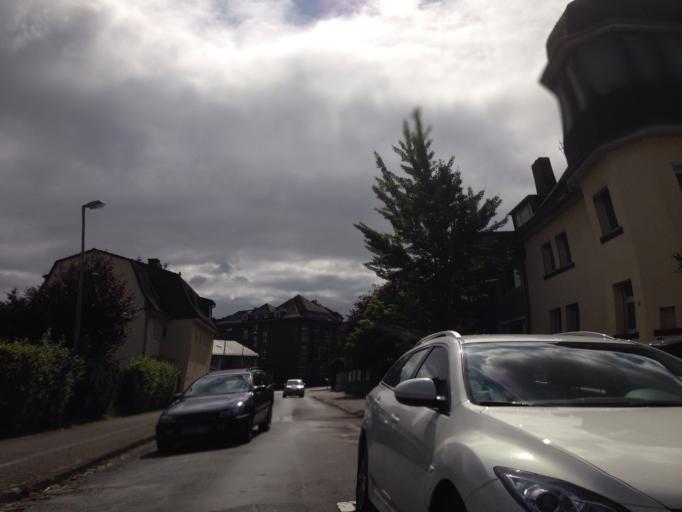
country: DE
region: Hesse
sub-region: Regierungsbezirk Giessen
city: Limburg an der Lahn
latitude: 50.3882
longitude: 8.0546
